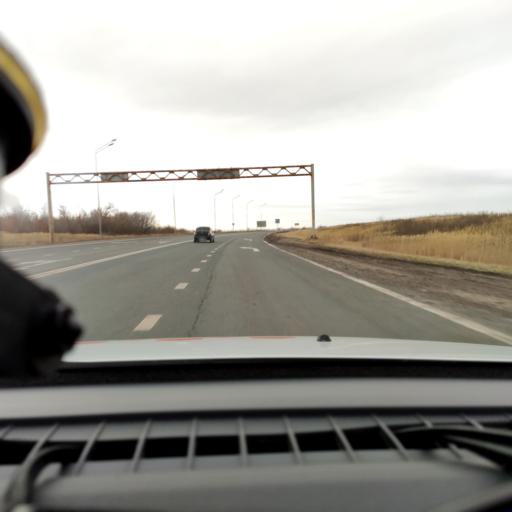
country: RU
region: Samara
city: Smyshlyayevka
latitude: 53.1445
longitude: 50.3904
